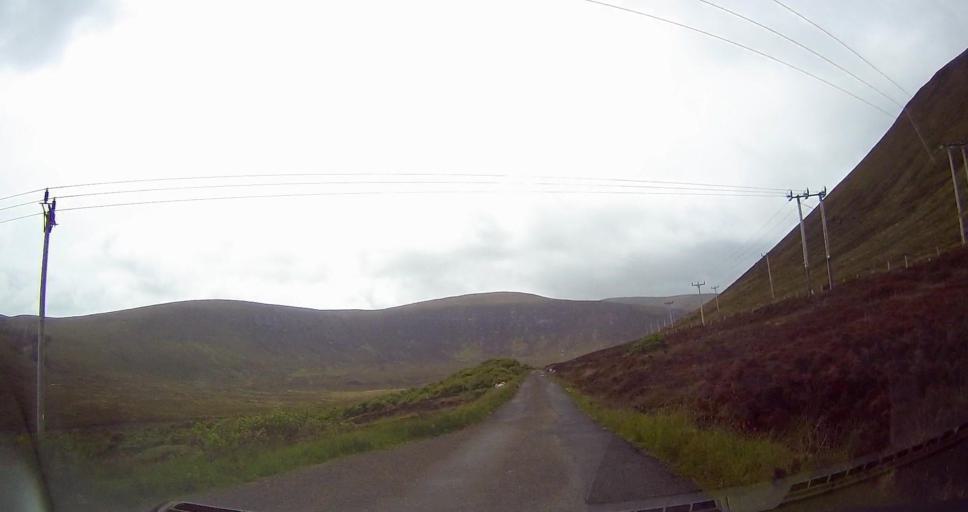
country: GB
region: Scotland
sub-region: Orkney Islands
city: Stromness
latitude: 58.8972
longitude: -3.3146
